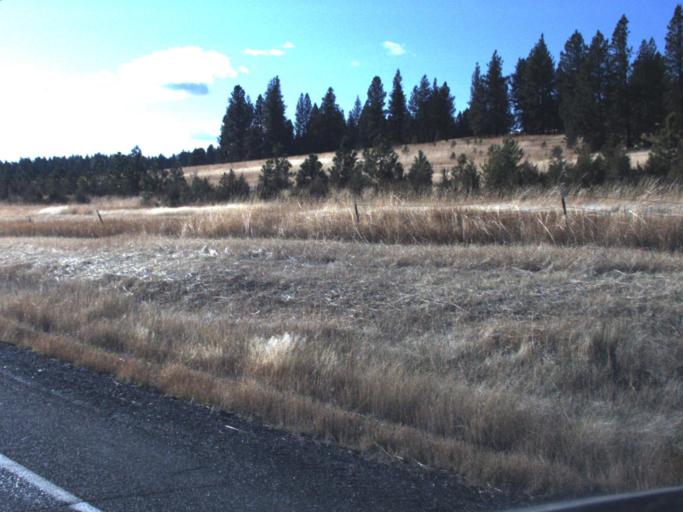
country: US
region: Washington
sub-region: Asotin County
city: Asotin
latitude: 46.1180
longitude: -117.1352
